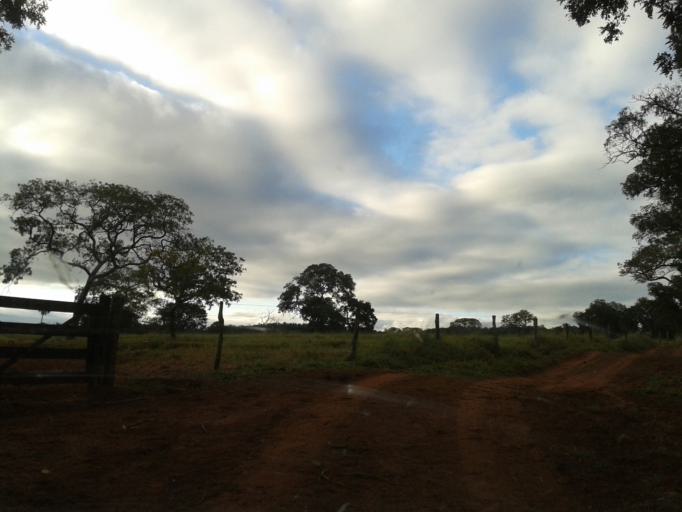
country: BR
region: Minas Gerais
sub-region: Campina Verde
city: Campina Verde
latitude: -19.4663
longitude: -49.6518
